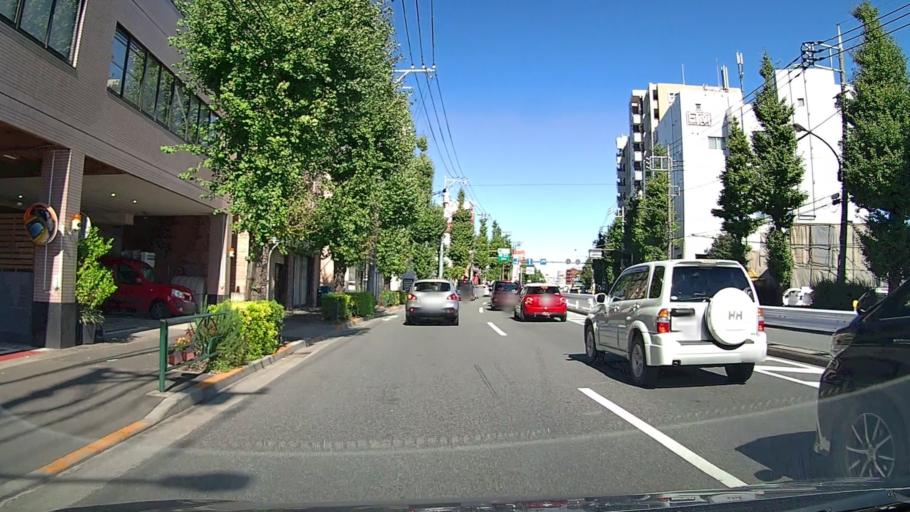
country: JP
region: Saitama
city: Wako
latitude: 35.7653
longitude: 139.6195
